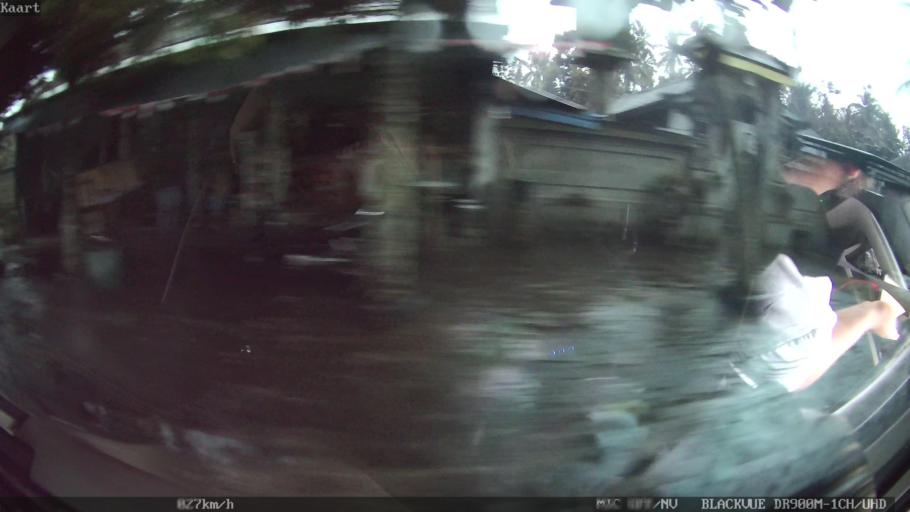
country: ID
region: Bali
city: Banjar Tengah
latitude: -8.4911
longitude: 115.1883
